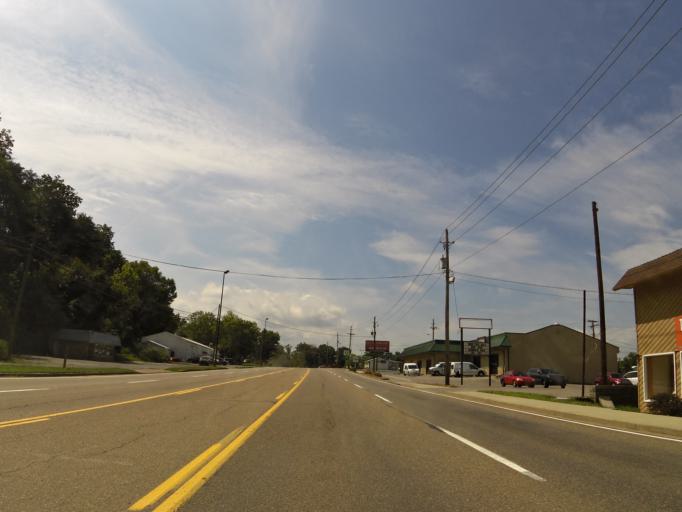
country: US
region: Tennessee
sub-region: Sullivan County
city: Kingsport
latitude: 36.5231
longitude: -82.5606
